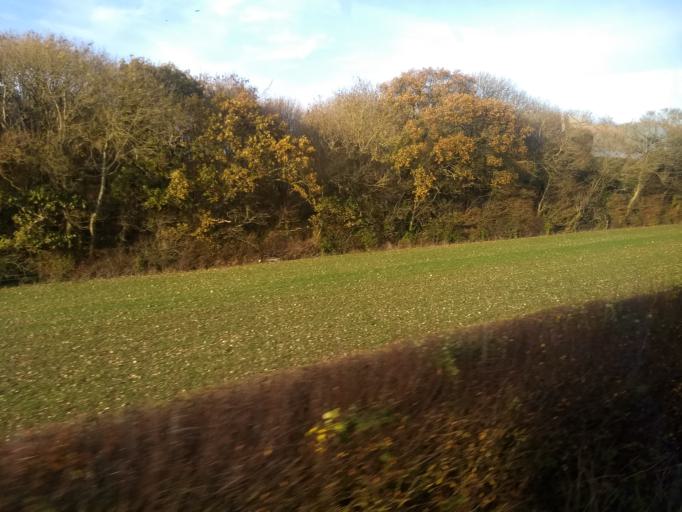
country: GB
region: England
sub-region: Isle of Wight
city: Shalfleet
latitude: 50.6824
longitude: -1.3887
